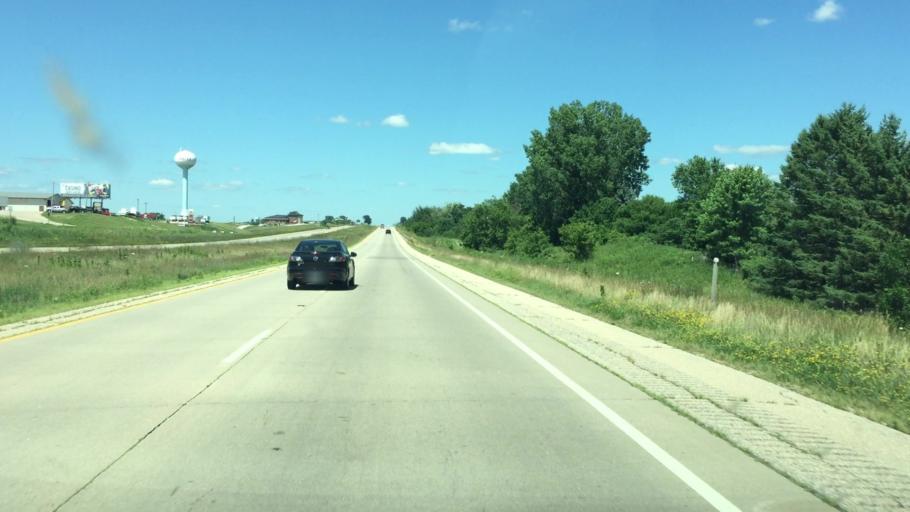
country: US
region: Wisconsin
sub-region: Grant County
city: Dickeyville
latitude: 42.5823
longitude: -90.6057
